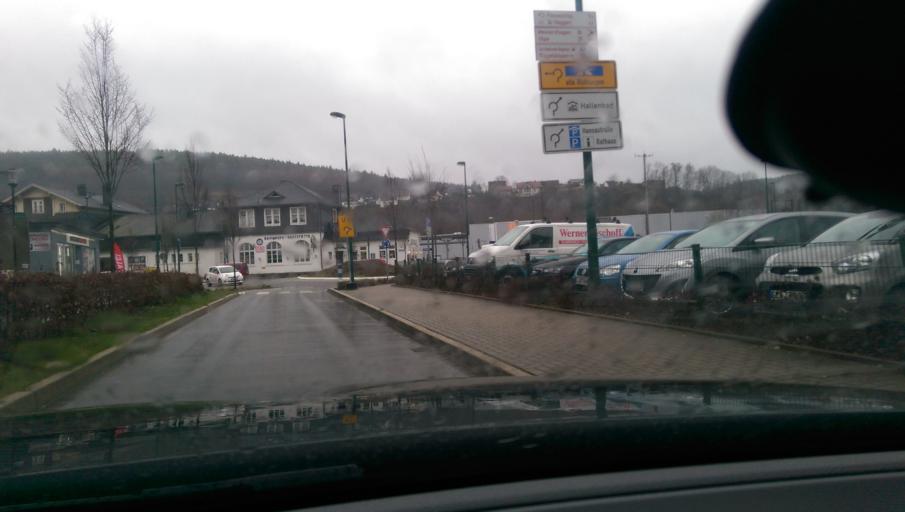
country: DE
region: North Rhine-Westphalia
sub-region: Regierungsbezirk Arnsberg
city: Attendorn
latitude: 51.1256
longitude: 7.9080
